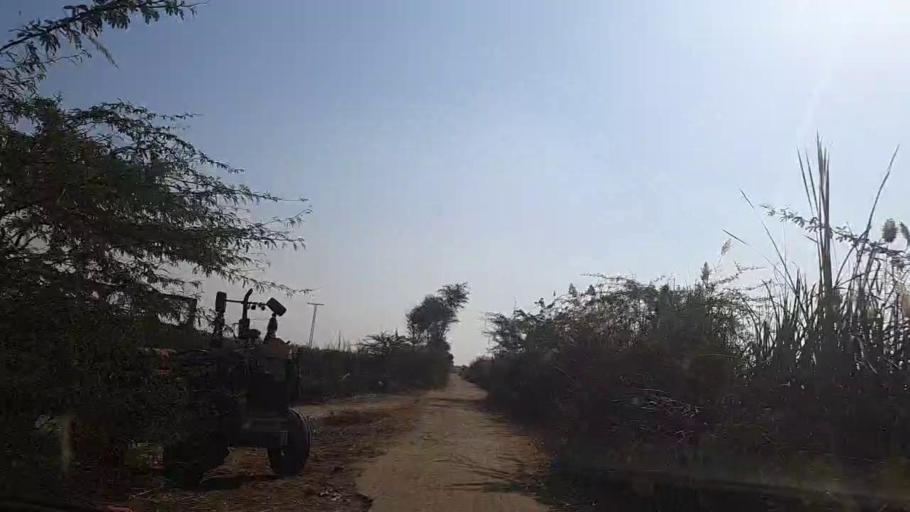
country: PK
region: Sindh
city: Sakrand
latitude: 26.0821
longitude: 68.3695
